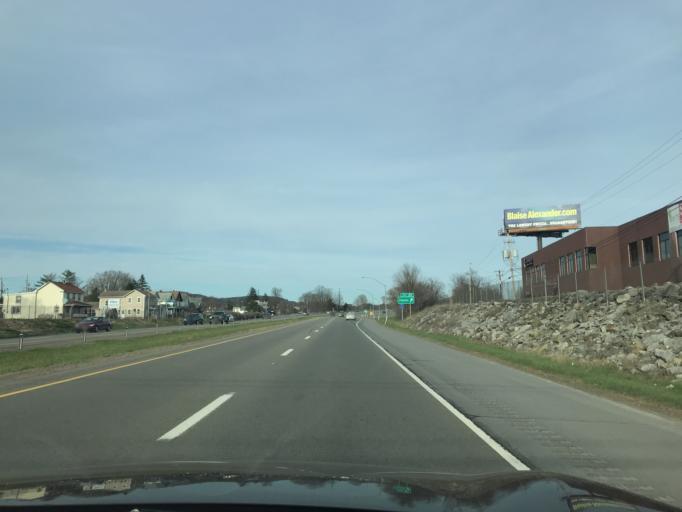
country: US
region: Pennsylvania
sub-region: Lycoming County
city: Faxon
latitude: 41.2472
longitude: -76.9850
